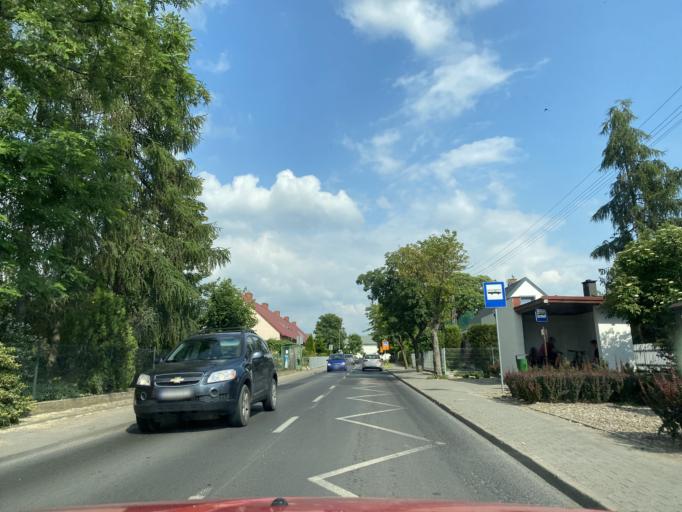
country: PL
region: Greater Poland Voivodeship
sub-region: Powiat poznanski
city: Dopiewo
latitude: 52.3600
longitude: 16.7084
